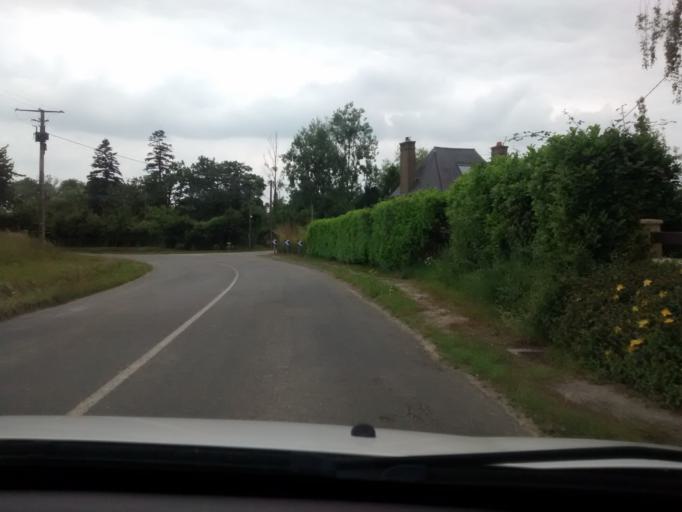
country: FR
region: Brittany
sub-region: Departement d'Ille-et-Vilaine
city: La Bouexiere
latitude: 48.1896
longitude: -1.4448
